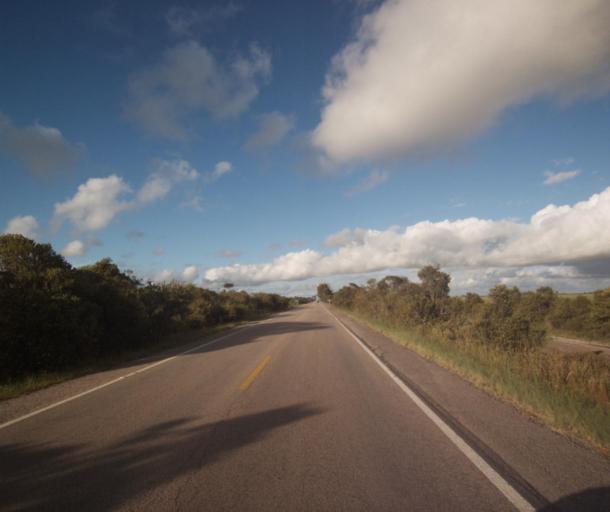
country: BR
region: Rio Grande do Sul
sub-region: Rio Grande
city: Rio Grande
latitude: -32.1822
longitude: -52.4246
